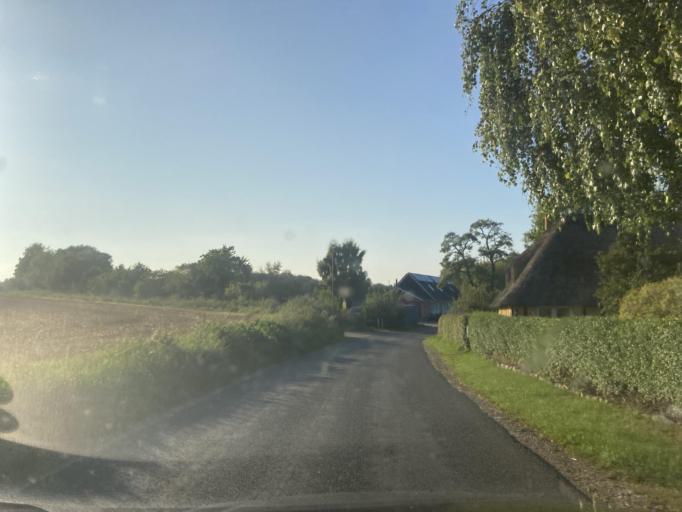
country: DK
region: South Denmark
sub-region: Svendborg Kommune
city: Thuro By
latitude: 55.1145
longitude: 10.7343
